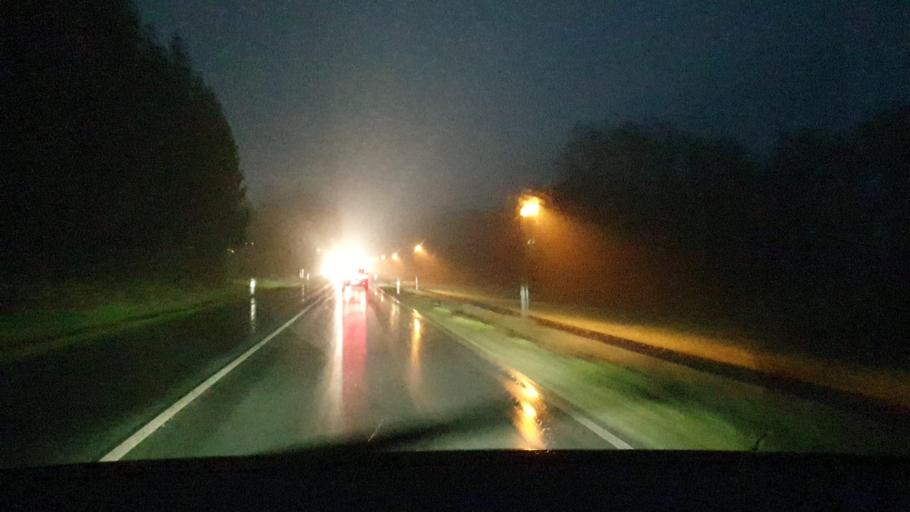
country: DE
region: Rheinland-Pfalz
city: Rennerod
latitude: 50.6136
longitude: 8.0708
